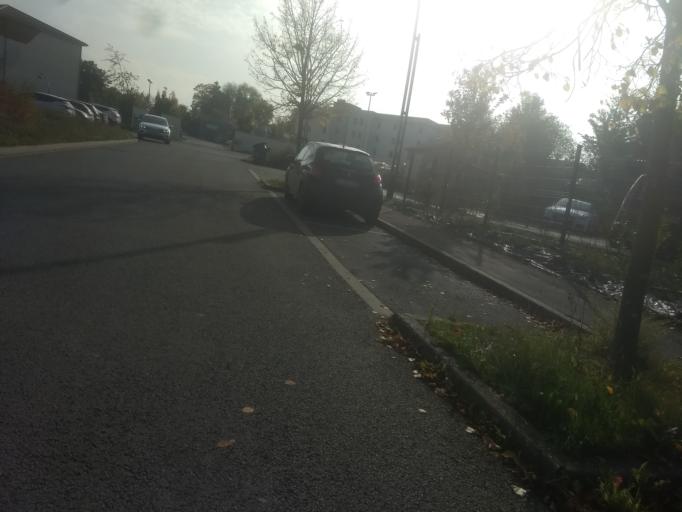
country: FR
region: Nord-Pas-de-Calais
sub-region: Departement du Pas-de-Calais
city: Arras
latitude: 50.2947
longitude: 2.7920
